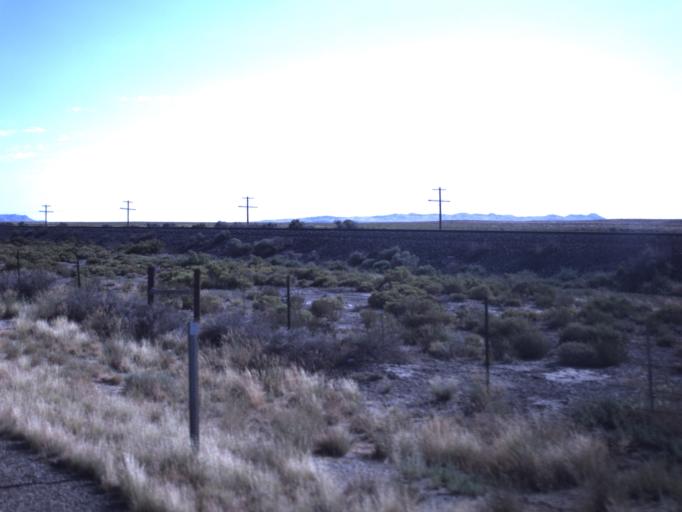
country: US
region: Utah
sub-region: Beaver County
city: Milford
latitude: 38.6332
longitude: -112.9840
